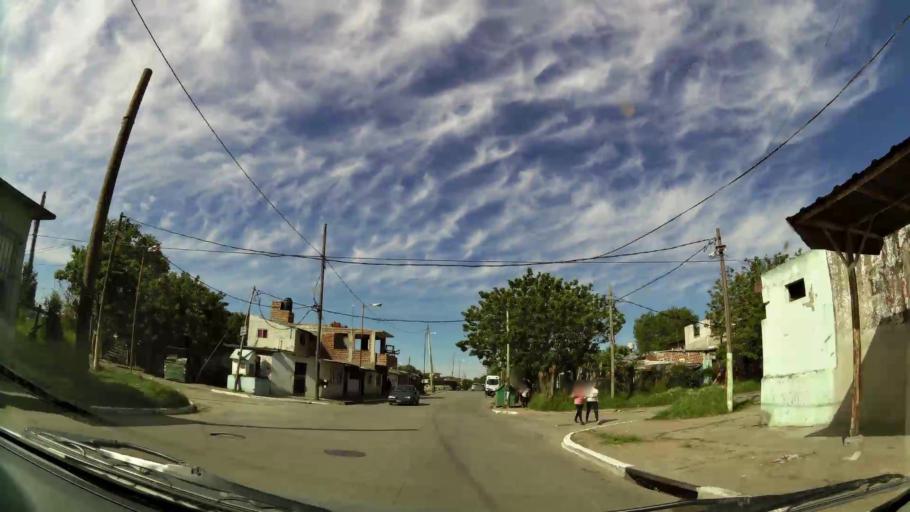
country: AR
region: Buenos Aires
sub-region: Partido de Quilmes
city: Quilmes
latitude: -34.7686
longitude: -58.3055
